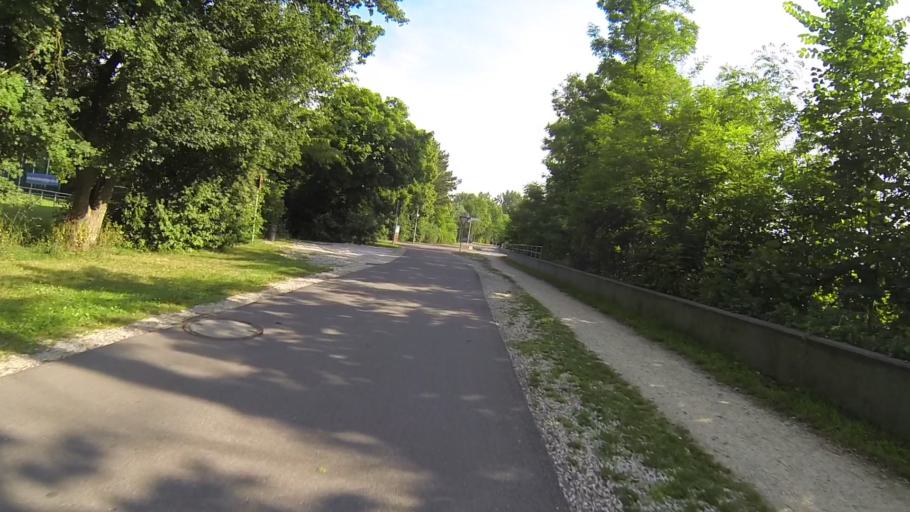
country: DE
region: Bavaria
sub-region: Swabia
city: Neu-Ulm
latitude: 48.4077
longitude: 10.0175
